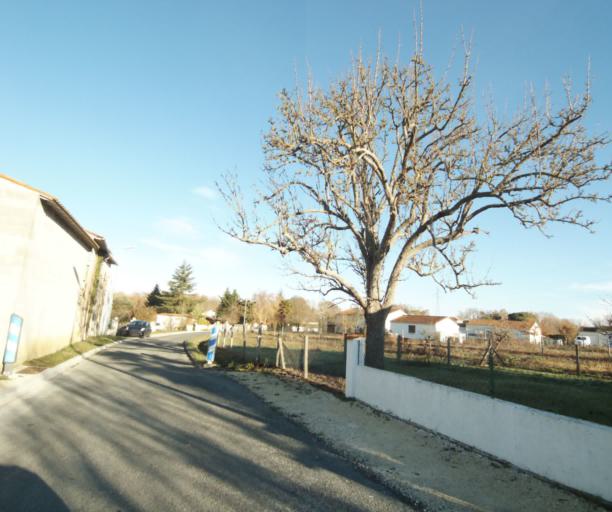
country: FR
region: Poitou-Charentes
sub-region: Departement de la Charente-Maritime
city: Fontcouverte
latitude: 45.7632
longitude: -0.6086
